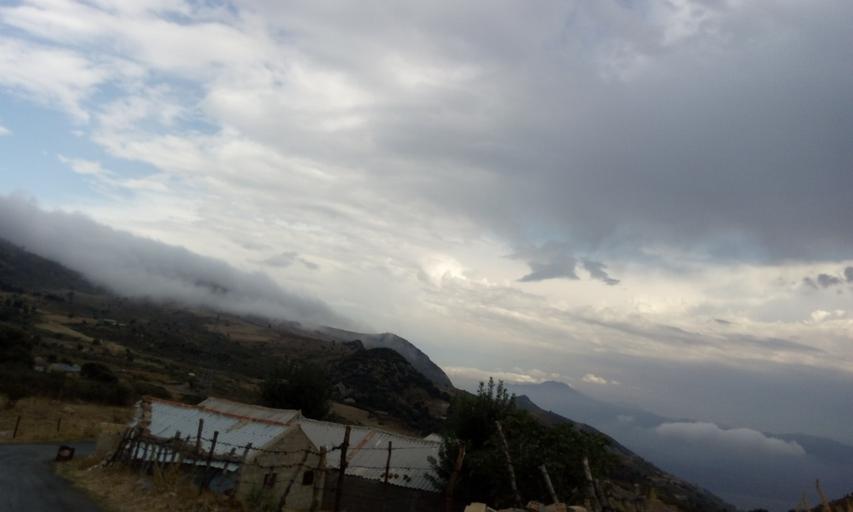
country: DZ
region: Tizi Ouzou
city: Chemini
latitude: 36.6093
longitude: 4.5609
